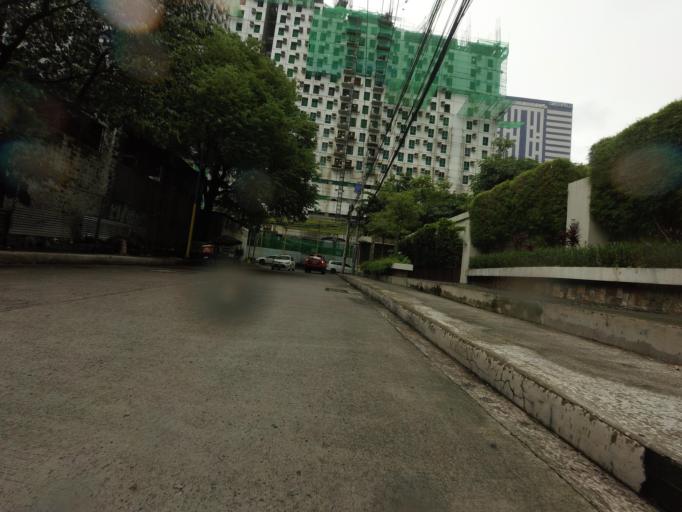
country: PH
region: Metro Manila
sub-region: Mandaluyong
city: Mandaluyong City
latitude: 14.5753
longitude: 121.0506
